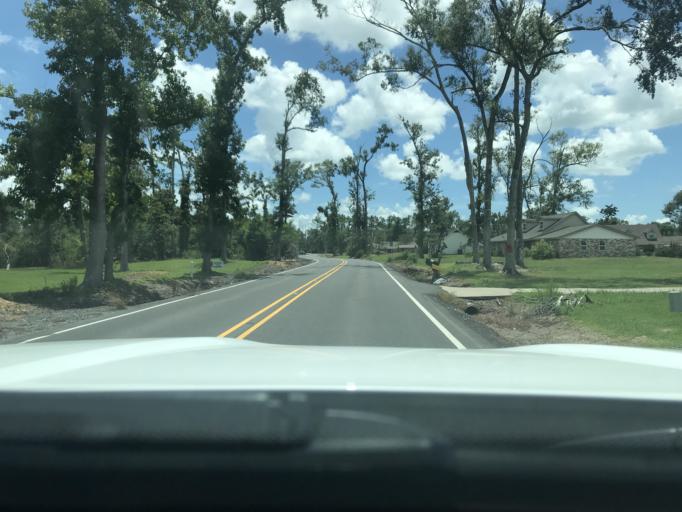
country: US
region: Louisiana
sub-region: Calcasieu Parish
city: Moss Bluff
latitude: 30.3104
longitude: -93.1832
